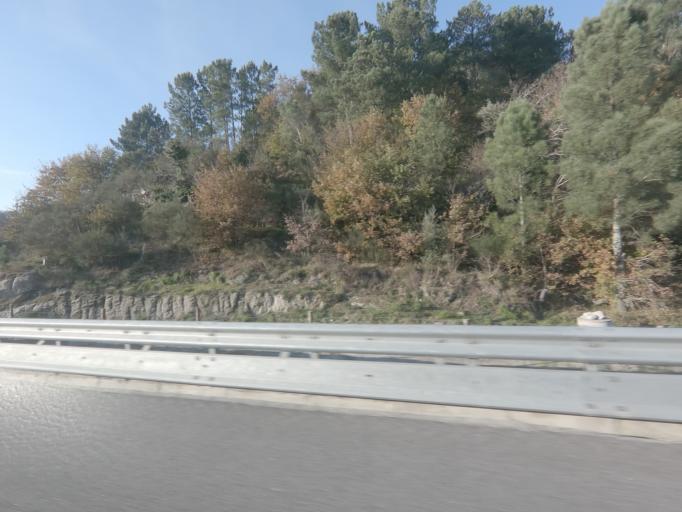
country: PT
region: Viseu
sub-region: Cinfaes
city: Cinfaes
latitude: 40.9866
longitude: -8.0558
